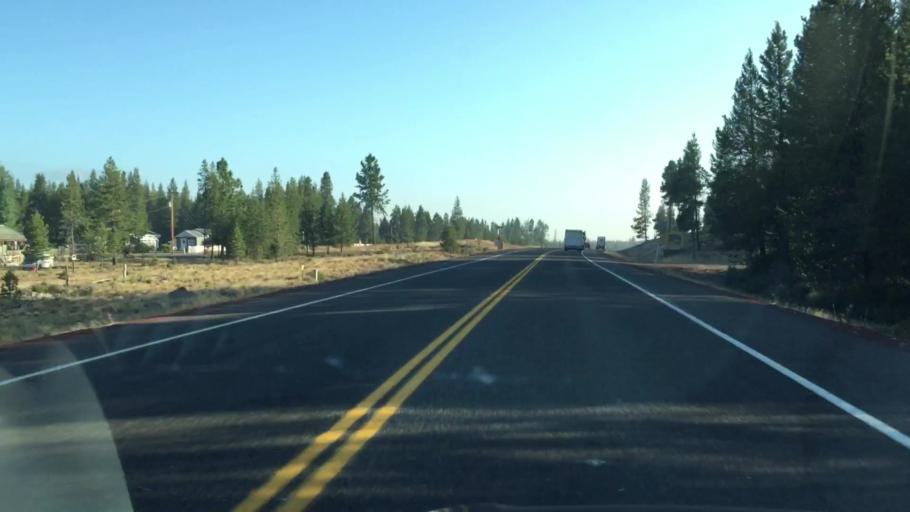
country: US
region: Oregon
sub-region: Deschutes County
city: La Pine
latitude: 43.4429
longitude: -121.7095
